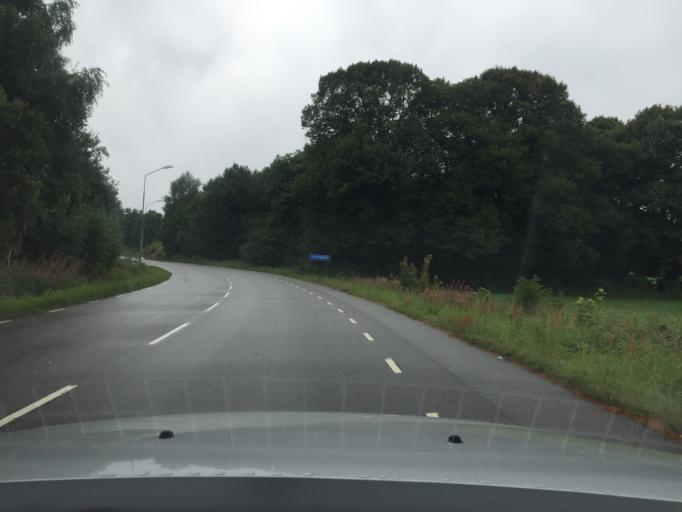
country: SE
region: Skane
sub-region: Hassleholms Kommun
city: Sosdala
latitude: 56.0079
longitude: 13.6450
